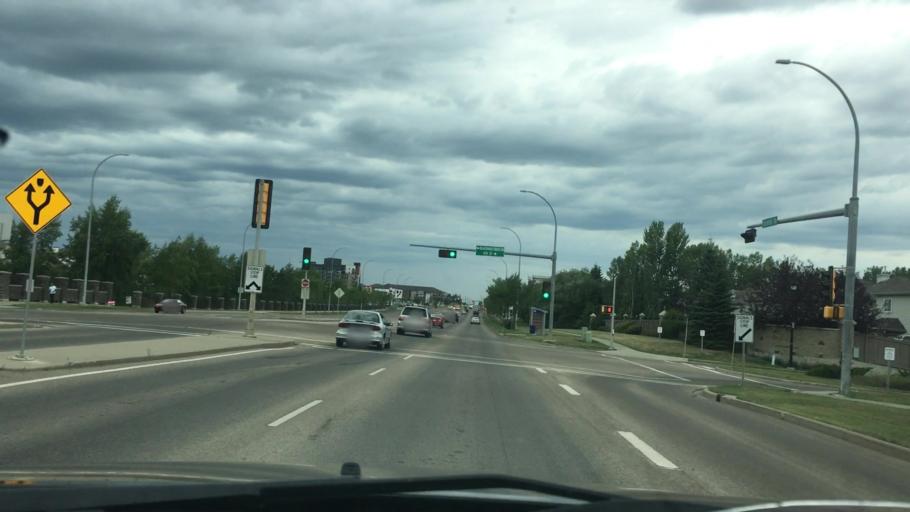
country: CA
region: Alberta
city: Beaumont
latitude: 53.4249
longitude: -113.5084
